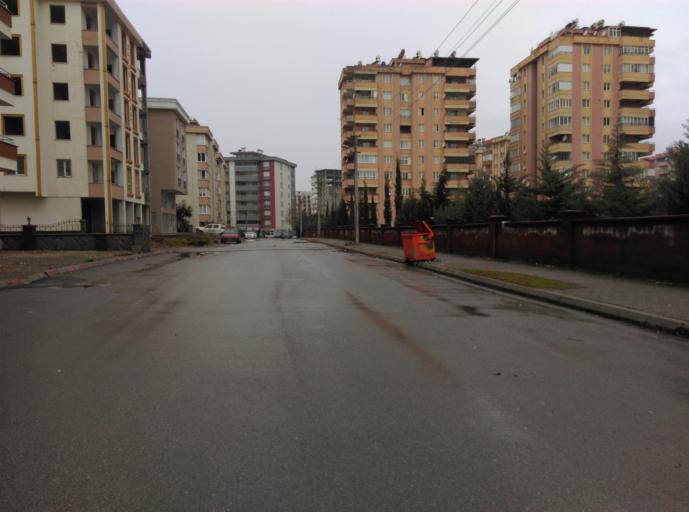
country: TR
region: Kahramanmaras
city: Kahramanmaras
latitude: 37.5837
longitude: 36.8983
